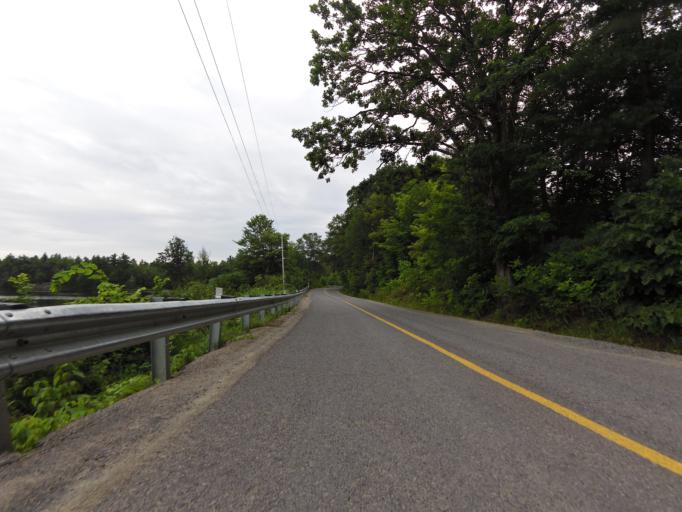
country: CA
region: Ontario
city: Kingston
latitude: 44.6520
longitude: -76.6544
